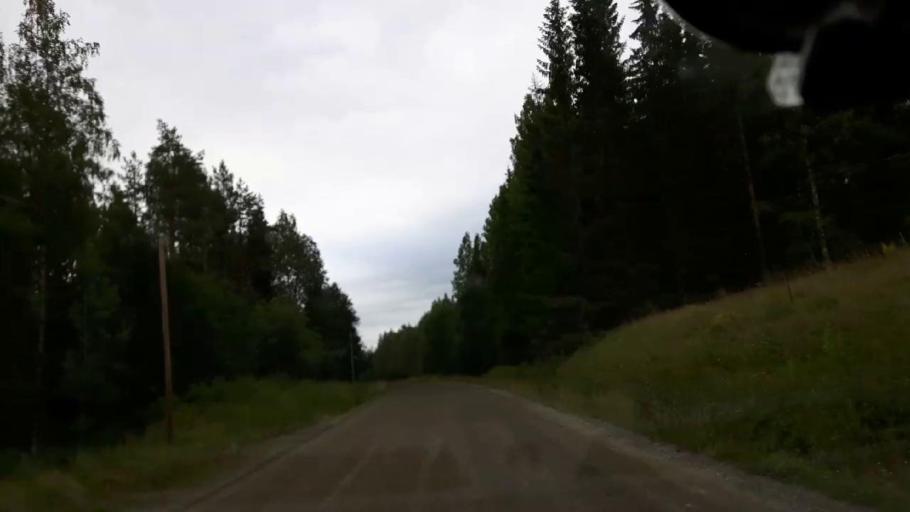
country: SE
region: Jaemtland
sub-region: Braecke Kommun
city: Braecke
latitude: 62.9060
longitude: 15.5931
